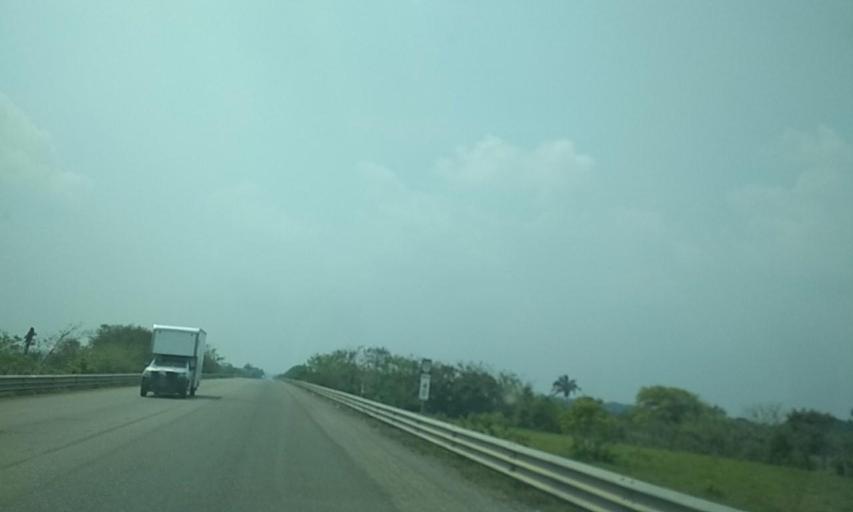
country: MX
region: Tabasco
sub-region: Huimanguillo
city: Francisco Rueda
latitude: 17.7754
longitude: -94.0477
